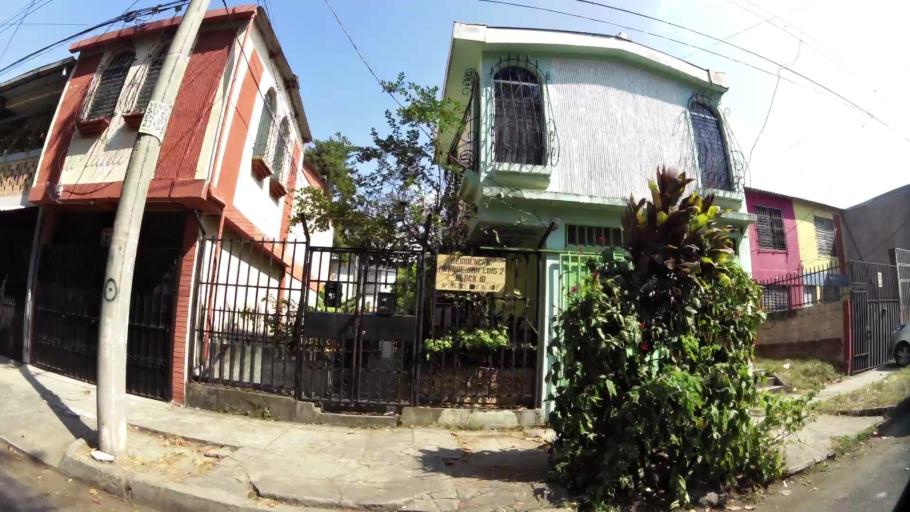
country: SV
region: San Salvador
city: Mejicanos
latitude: 13.7195
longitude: -89.2148
